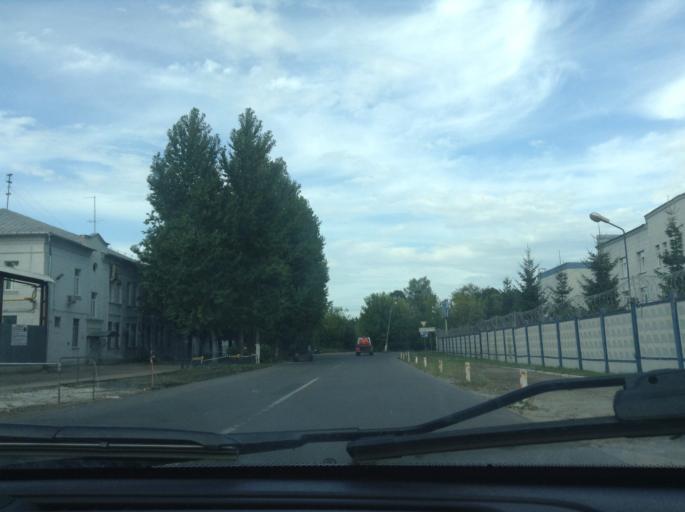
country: RU
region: Moskovskaya
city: Il'inskiy
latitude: 55.6108
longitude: 38.1105
